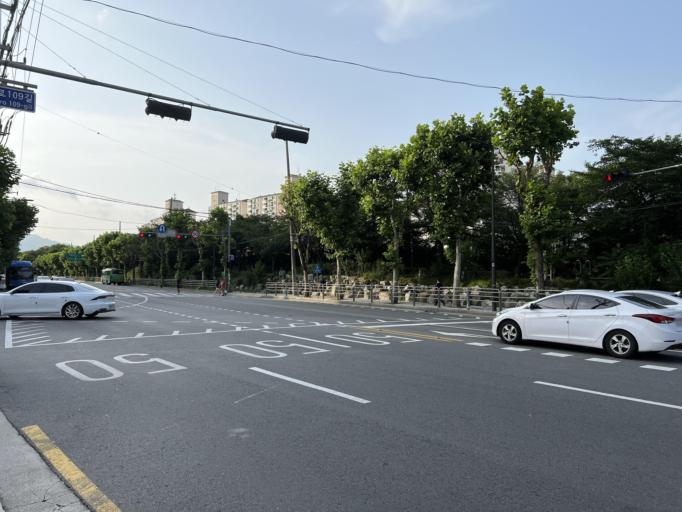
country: KR
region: Seoul
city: Seoul
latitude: 37.6308
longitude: 127.0412
